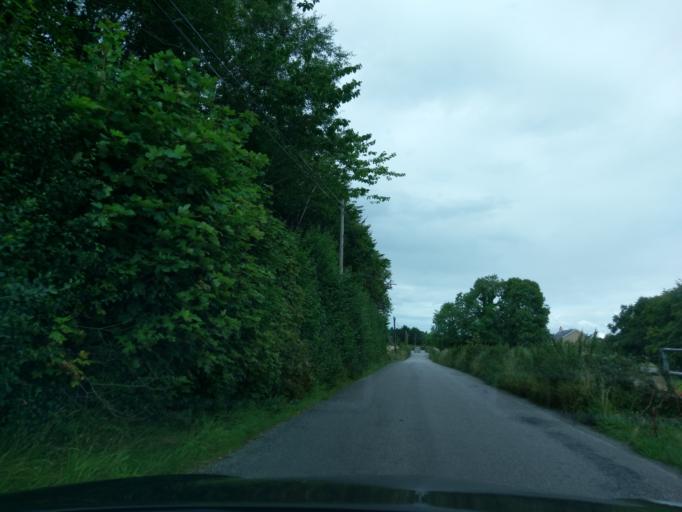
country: IE
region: Connaught
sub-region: County Galway
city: Gort
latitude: 53.1569
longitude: -8.7452
